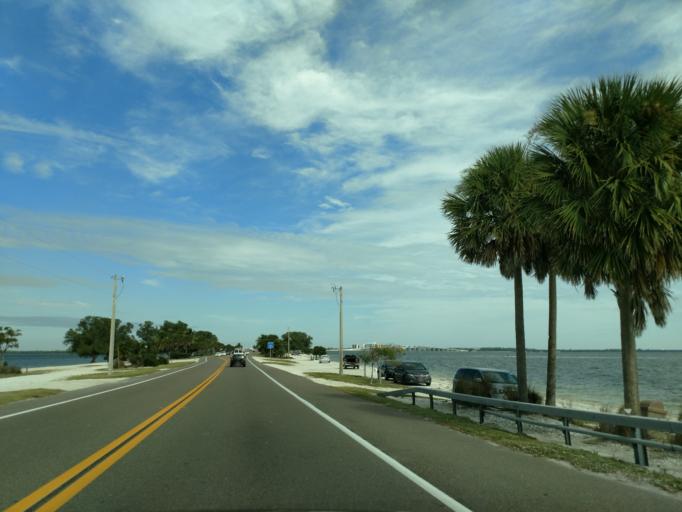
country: US
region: Florida
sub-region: Lee County
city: Sanibel
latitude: 26.4649
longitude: -82.0311
